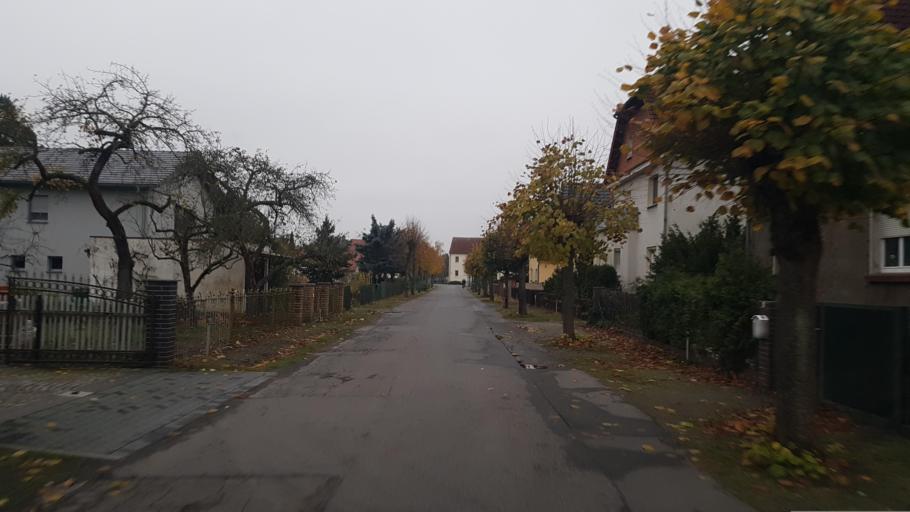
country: DE
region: Brandenburg
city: Ruhland
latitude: 51.4527
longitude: 13.8694
